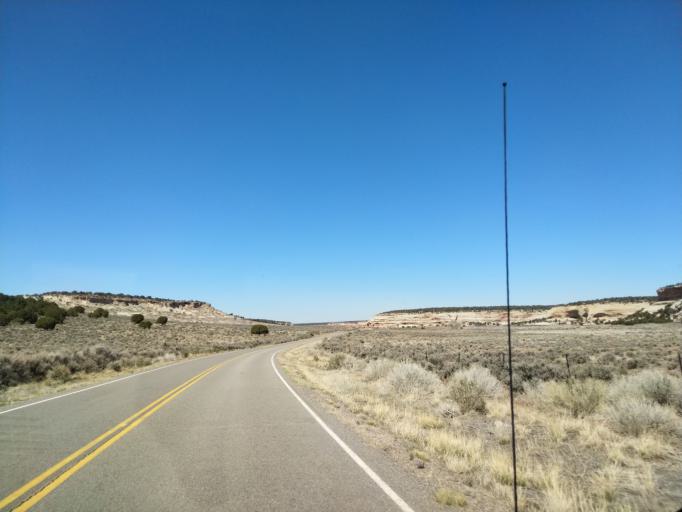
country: US
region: Colorado
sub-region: Mesa County
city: Fruita
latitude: 38.9841
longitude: -108.8088
